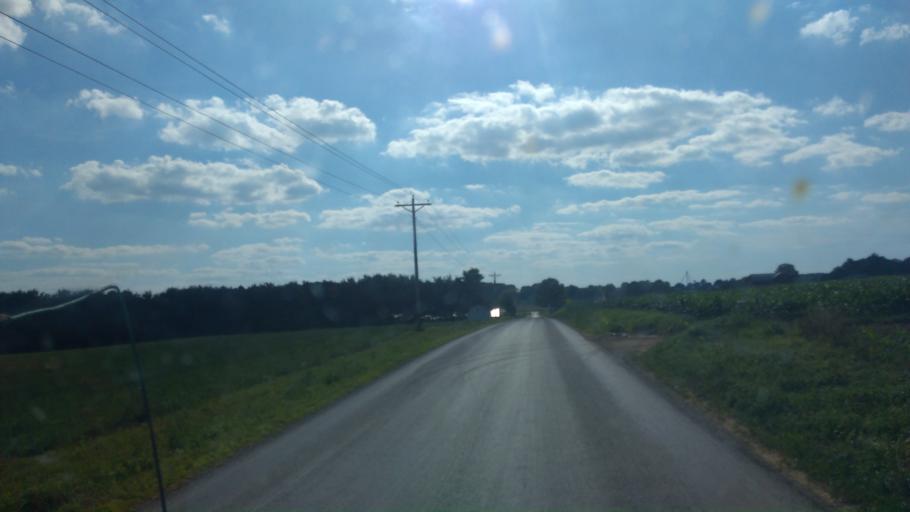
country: US
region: Ohio
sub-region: Wayne County
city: Apple Creek
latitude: 40.7262
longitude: -81.8704
